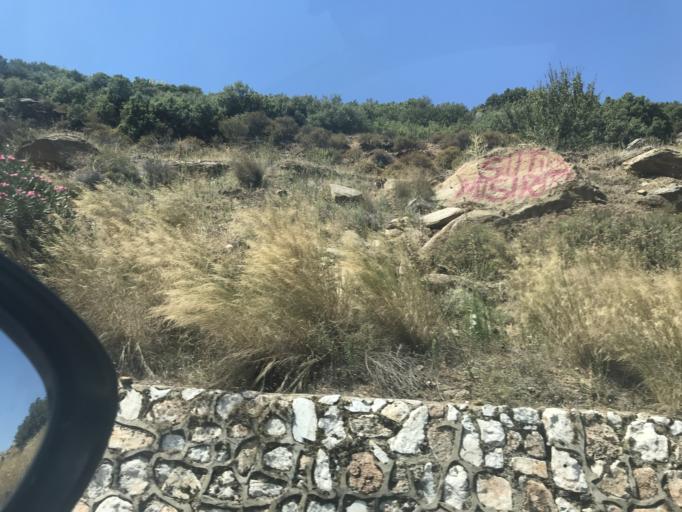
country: TR
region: Aydin
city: Akcaova
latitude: 37.5084
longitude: 28.1015
